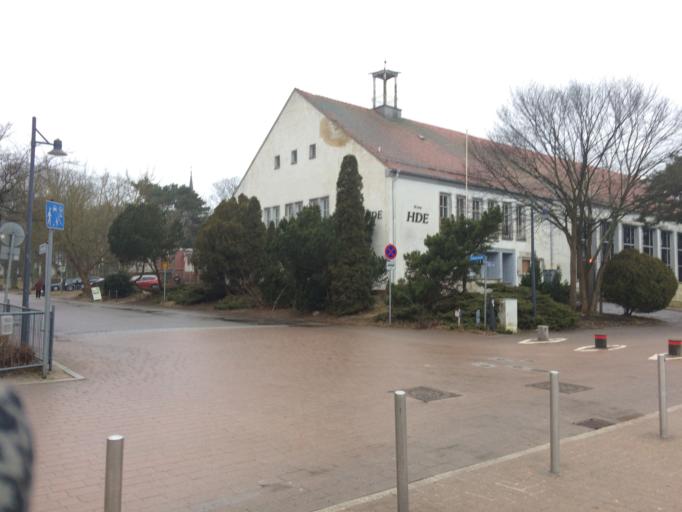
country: DE
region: Mecklenburg-Vorpommern
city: Seebad Heringsdorf
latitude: 53.9405
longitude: 14.1932
